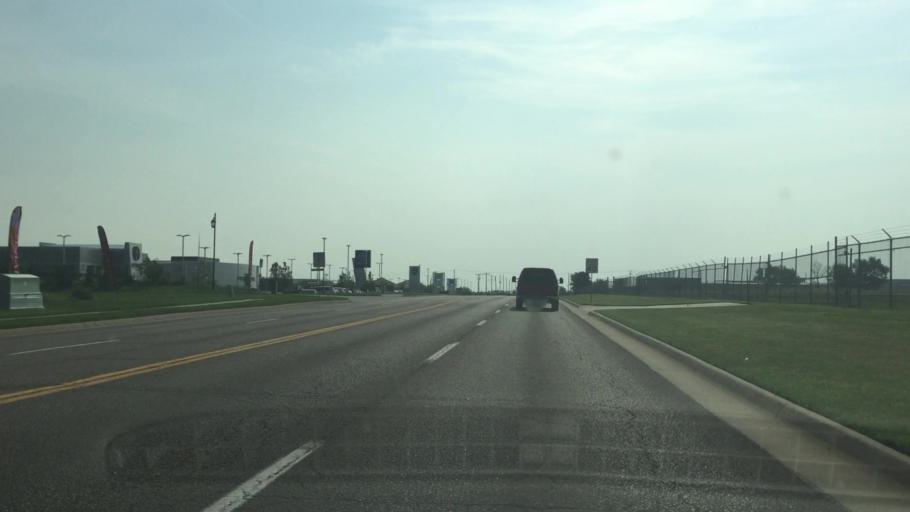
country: US
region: Kansas
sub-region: Sedgwick County
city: Bellaire
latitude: 37.7085
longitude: -97.2131
